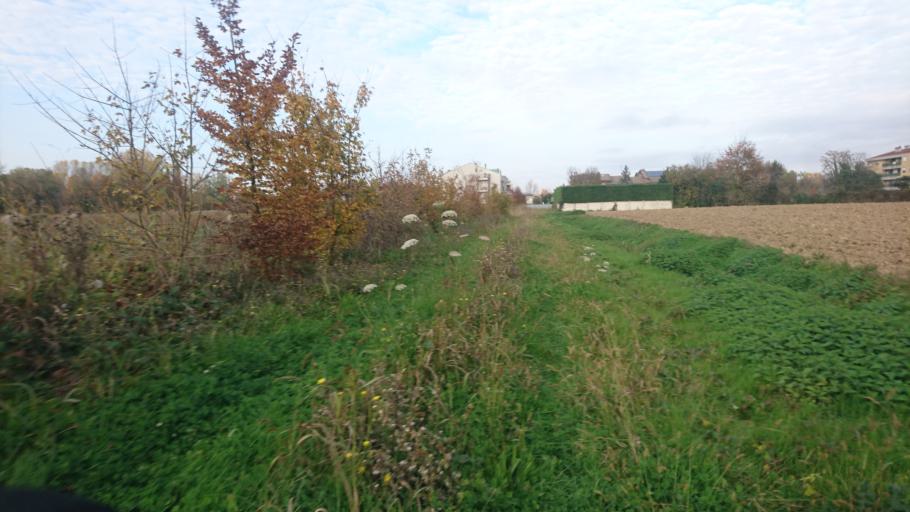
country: IT
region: Veneto
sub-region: Provincia di Padova
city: Mandriola-Sant'Agostino
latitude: 45.3839
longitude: 11.8461
